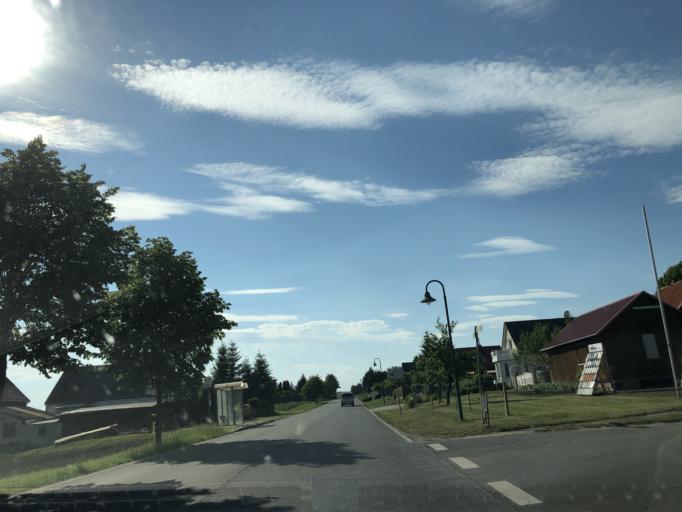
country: DE
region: Brandenburg
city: Angermunde
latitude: 53.0880
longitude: 13.9434
